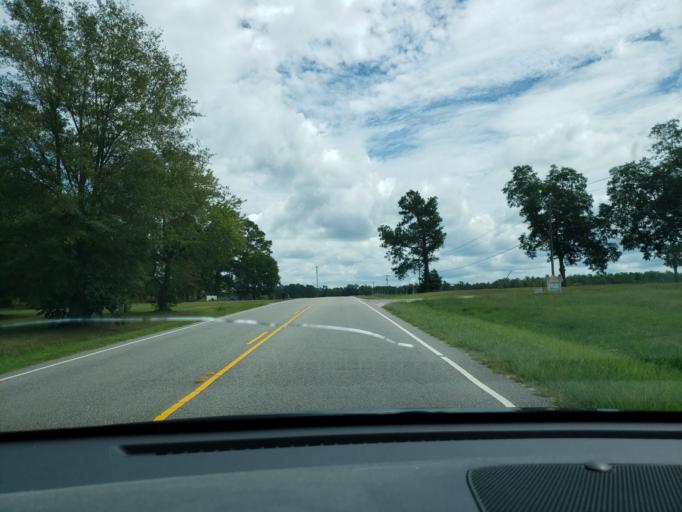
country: US
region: North Carolina
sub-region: Columbus County
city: Tabor City
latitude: 34.1876
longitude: -78.7821
